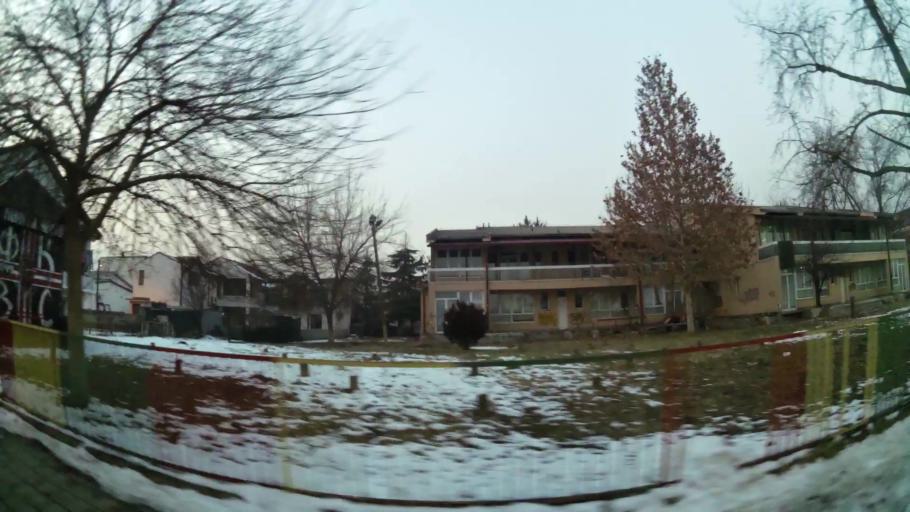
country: MK
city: Creshevo
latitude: 42.0103
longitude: 21.5124
